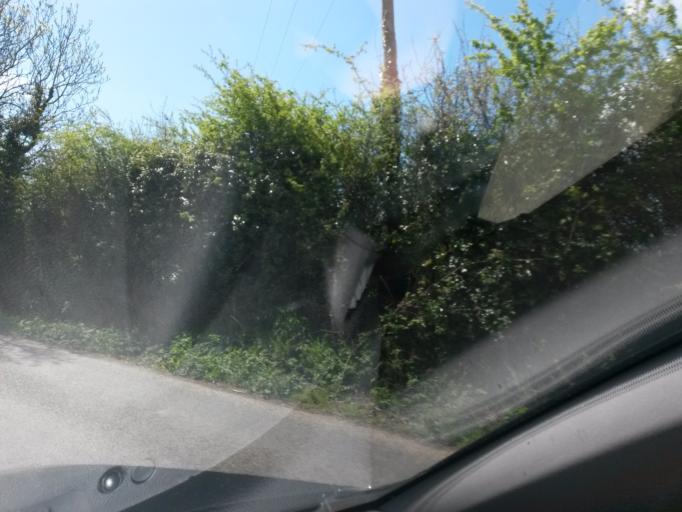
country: IE
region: Munster
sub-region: Waterford
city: Dunmore East
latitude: 52.2452
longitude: -6.8612
